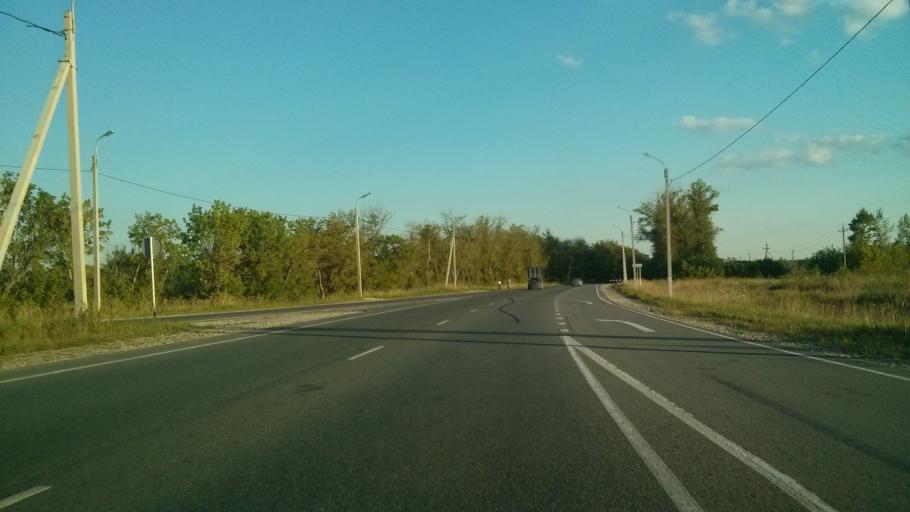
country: RU
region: Vladimir
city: Murom
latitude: 55.6151
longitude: 42.0258
